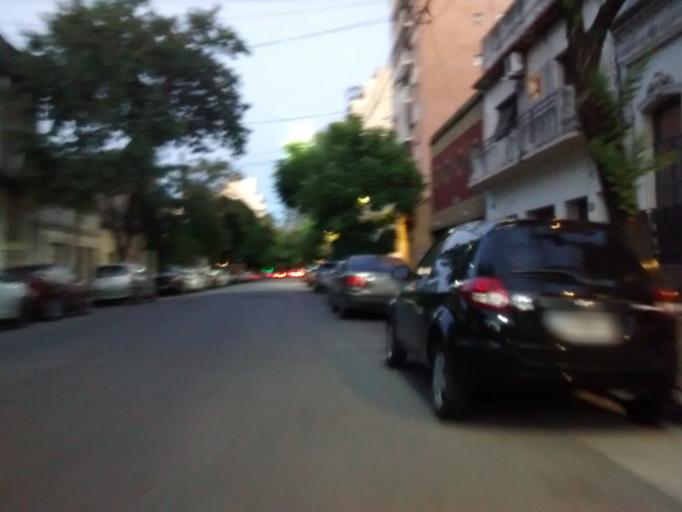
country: AR
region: Buenos Aires F.D.
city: Villa Santa Rita
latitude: -34.6103
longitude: -58.4479
